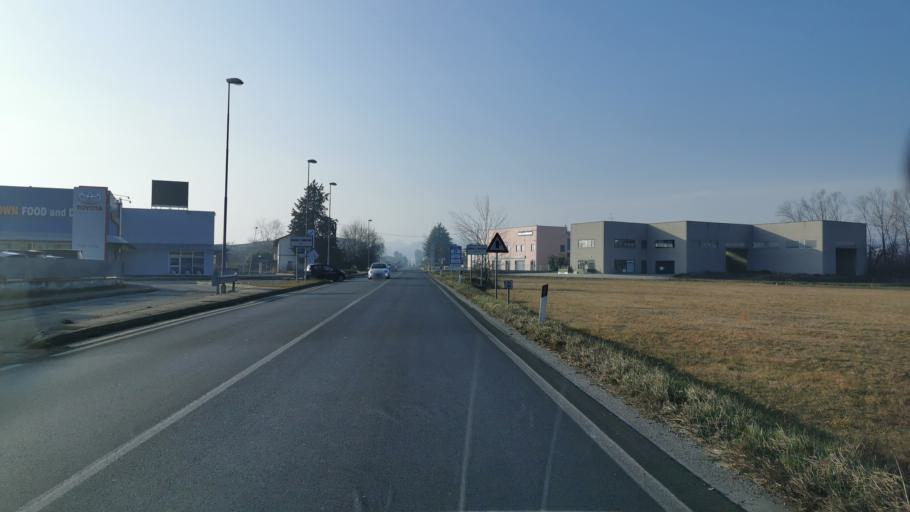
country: IT
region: Piedmont
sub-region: Provincia di Cuneo
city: Cinzano
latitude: 44.6957
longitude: 7.8984
